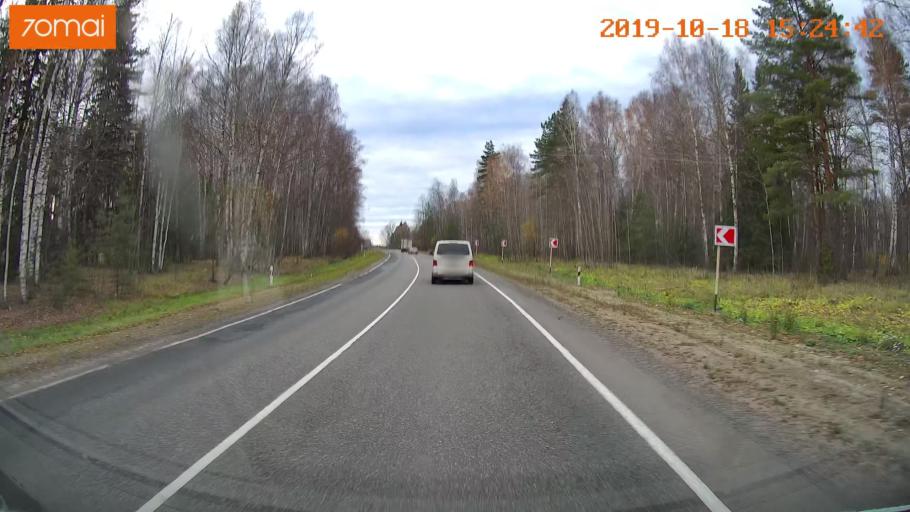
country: RU
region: Vladimir
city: Anopino
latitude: 55.7366
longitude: 40.7193
